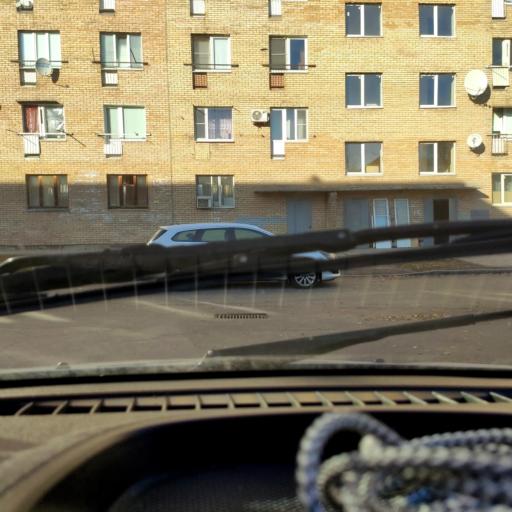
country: RU
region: Samara
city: Tol'yatti
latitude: 53.5110
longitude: 49.4526
